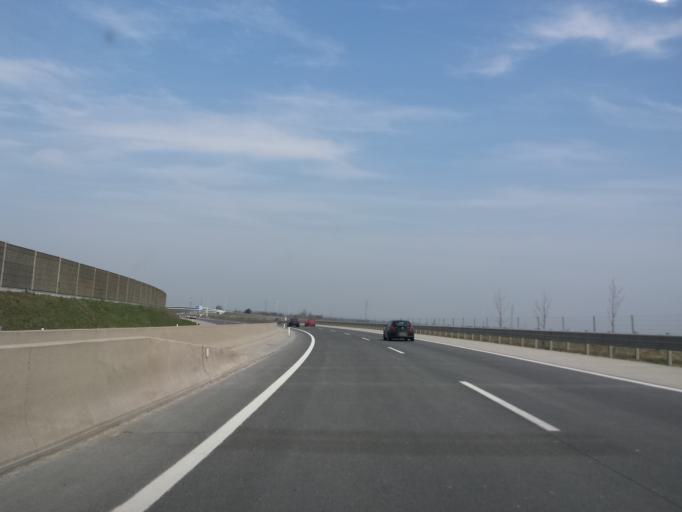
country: AT
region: Lower Austria
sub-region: Politischer Bezirk Ganserndorf
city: Aderklaa
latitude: 48.2703
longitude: 16.5047
